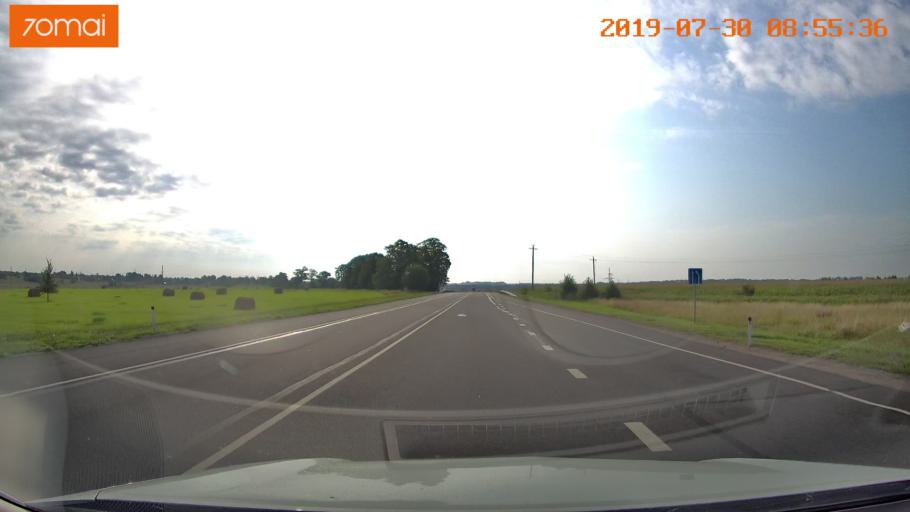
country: RU
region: Kaliningrad
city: Gusev
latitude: 54.6008
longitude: 22.0548
